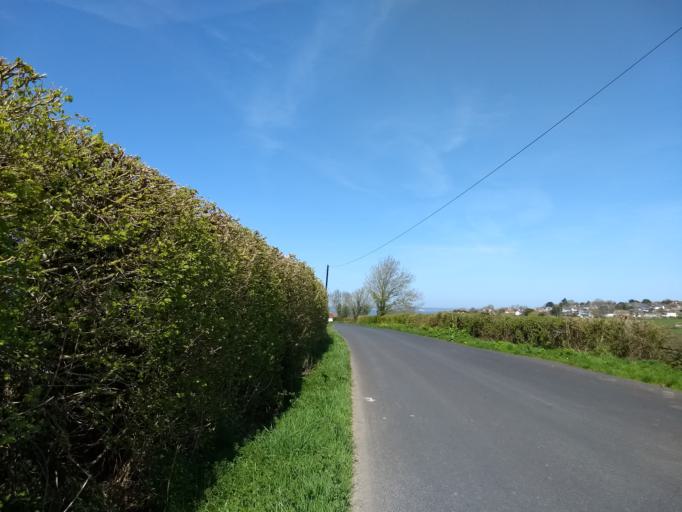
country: GB
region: England
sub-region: Isle of Wight
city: Gurnard
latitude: 50.7507
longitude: -1.3325
